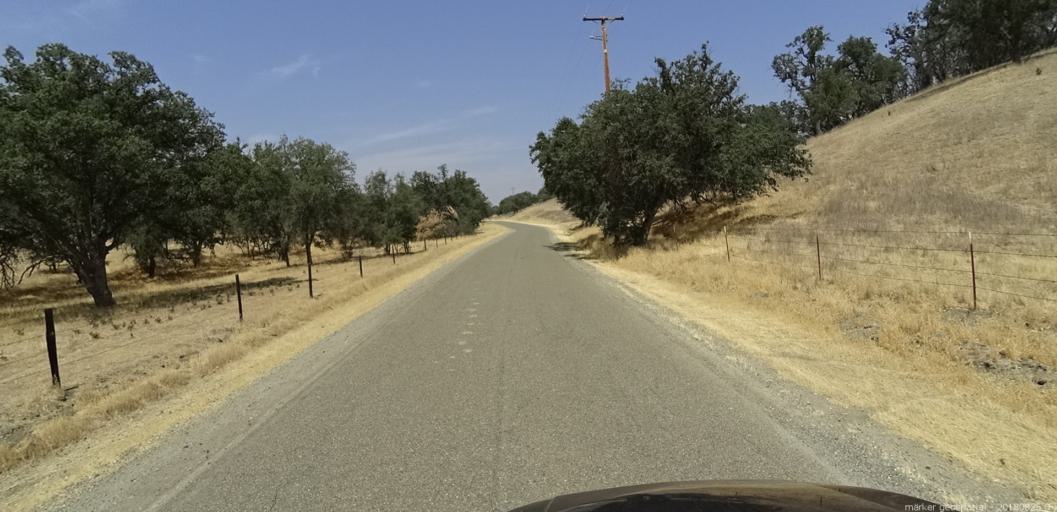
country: US
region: California
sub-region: San Luis Obispo County
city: Shandon
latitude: 35.8596
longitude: -120.3933
